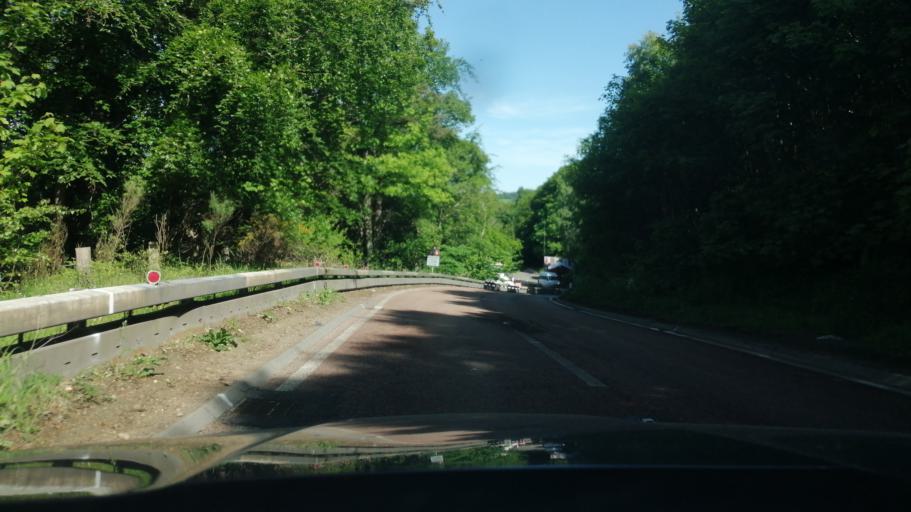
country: GB
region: Scotland
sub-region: Moray
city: Rothes
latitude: 57.4897
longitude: -3.1800
